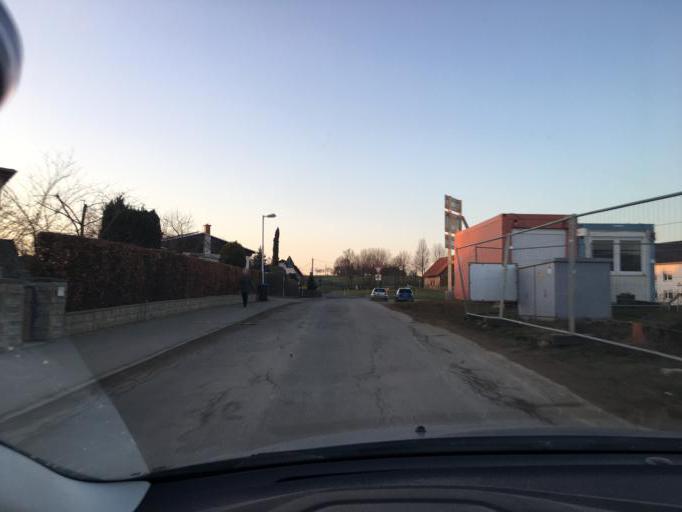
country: DE
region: Saxony
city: Lunzenau
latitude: 50.9654
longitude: 12.7503
